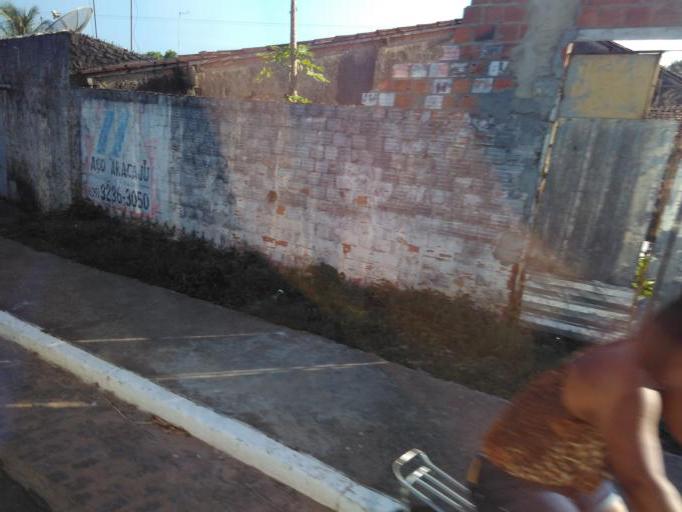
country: BR
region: Sergipe
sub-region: Laranjeiras
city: Laranjeiras
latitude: -10.7355
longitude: -37.1845
